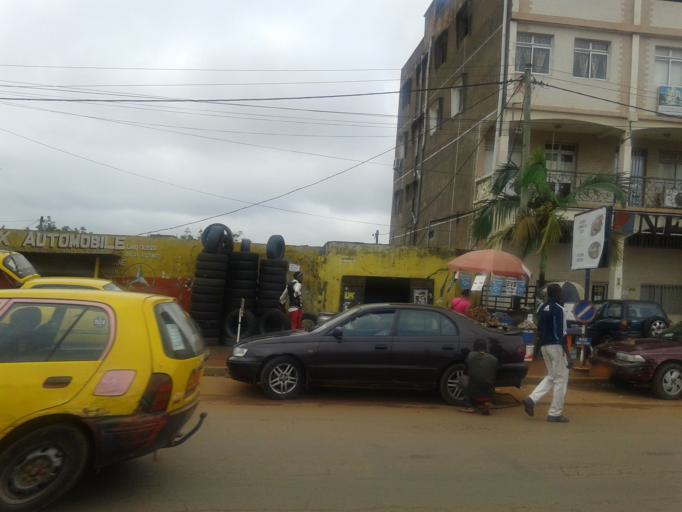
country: CM
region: Centre
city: Yaounde
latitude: 3.8626
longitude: 11.5254
